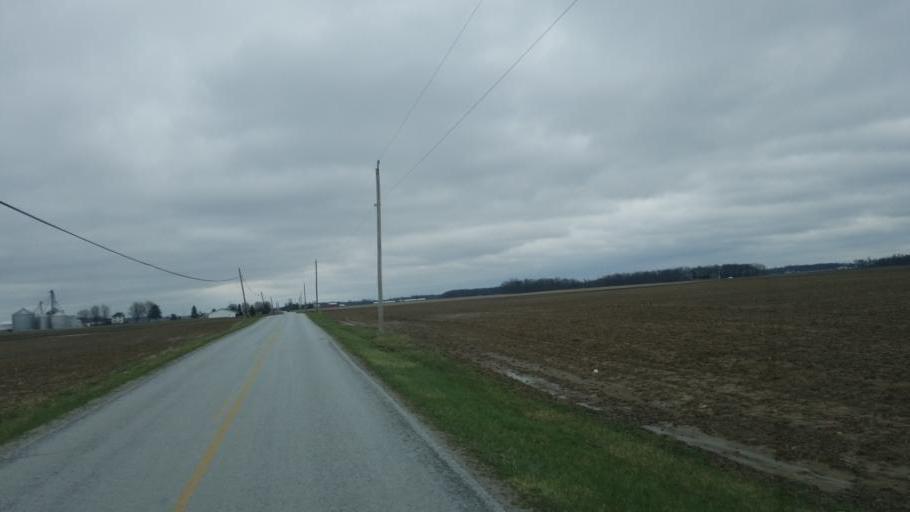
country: US
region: Ohio
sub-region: Hardin County
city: Kenton
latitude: 40.6580
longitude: -83.5205
